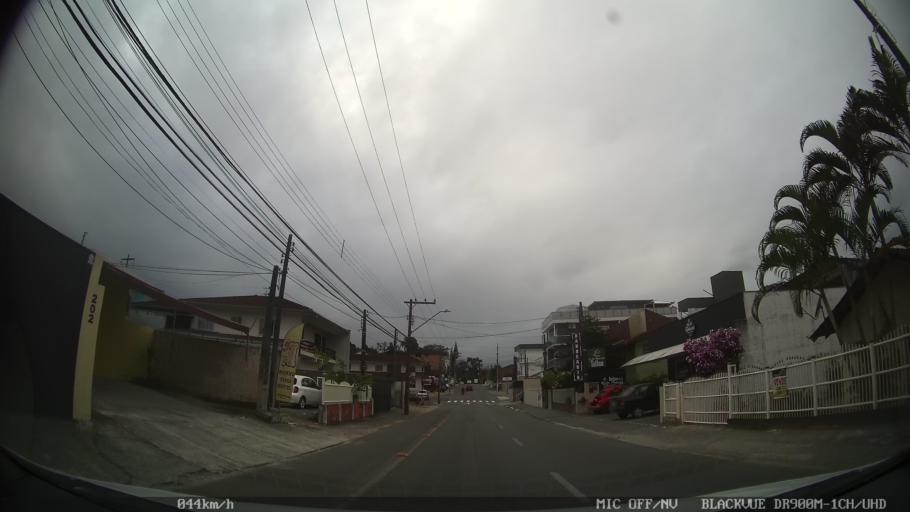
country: BR
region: Santa Catarina
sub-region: Joinville
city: Joinville
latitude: -26.2756
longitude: -48.8743
